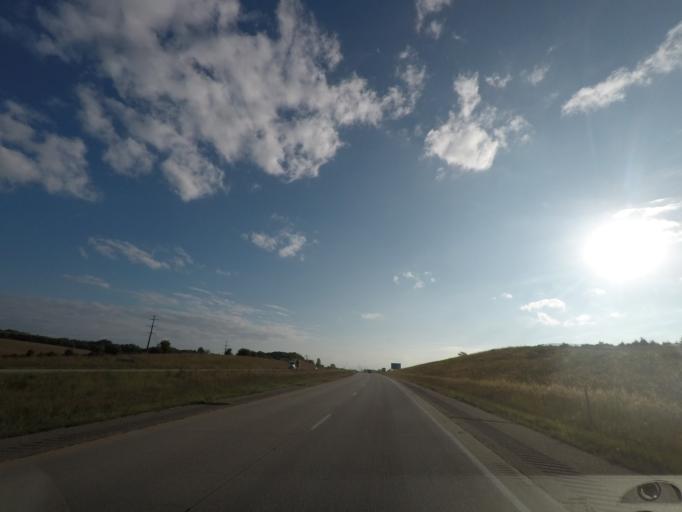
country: US
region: Iowa
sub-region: Warren County
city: Norwalk
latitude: 41.4991
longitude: -93.6029
